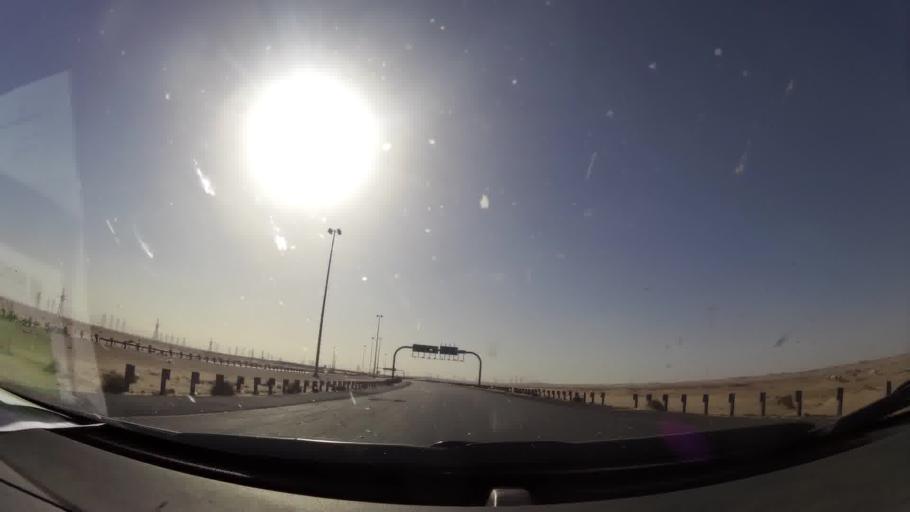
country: KW
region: Al Asimah
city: Kuwait City
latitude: 29.6430
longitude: 47.9428
